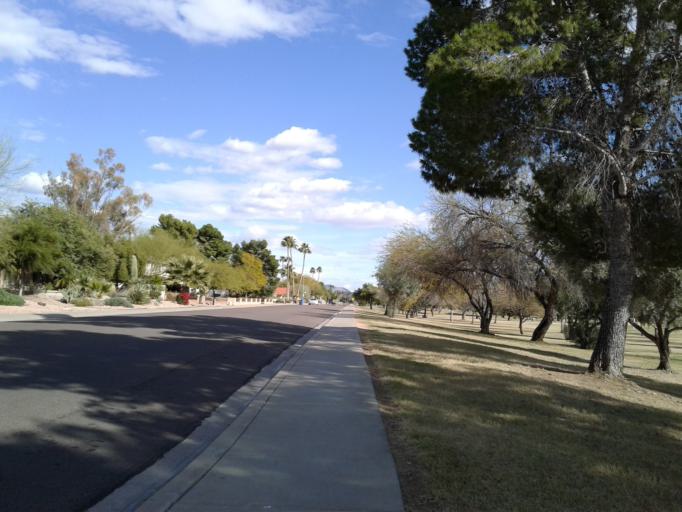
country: US
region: Arizona
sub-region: Maricopa County
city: Paradise Valley
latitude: 33.6079
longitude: -111.9598
